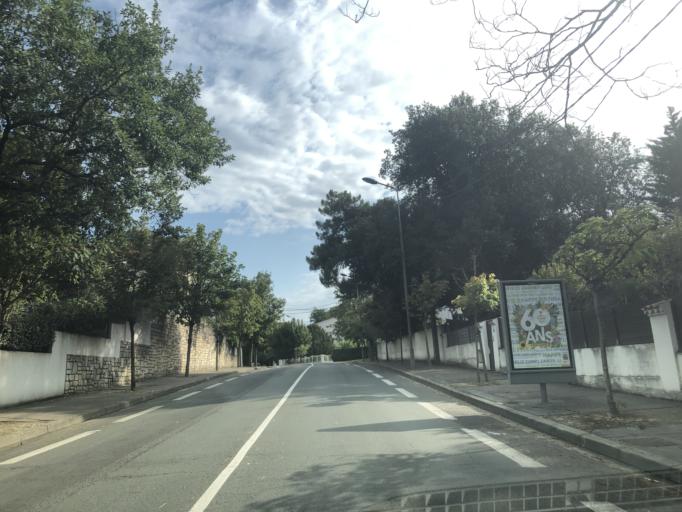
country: FR
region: Poitou-Charentes
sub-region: Departement de la Charente-Maritime
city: Royan
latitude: 45.6266
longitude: -1.0437
